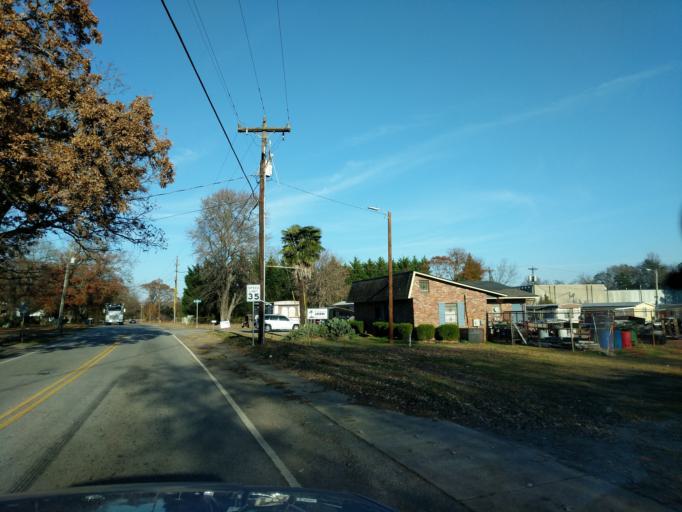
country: US
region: South Carolina
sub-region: Spartanburg County
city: Fairforest
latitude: 34.9533
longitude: -82.0179
